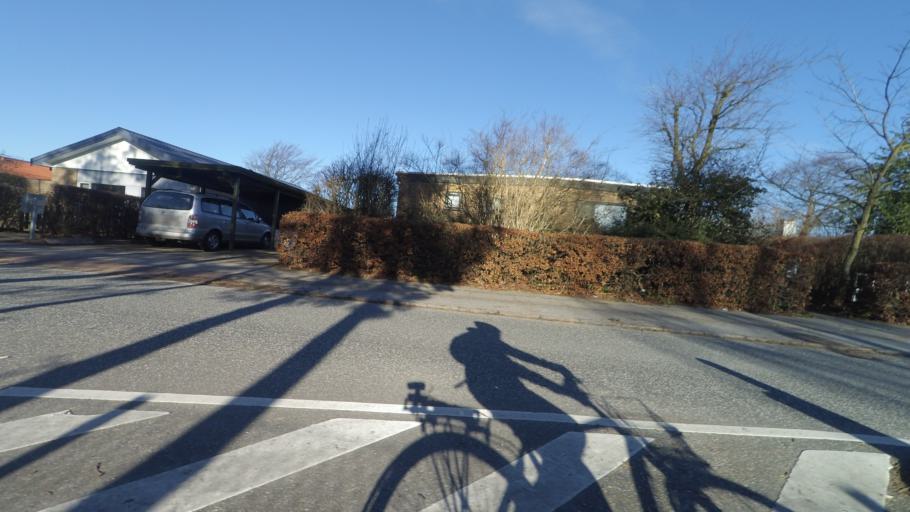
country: DK
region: Central Jutland
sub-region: Arhus Kommune
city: Kolt
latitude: 56.1070
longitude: 10.0955
